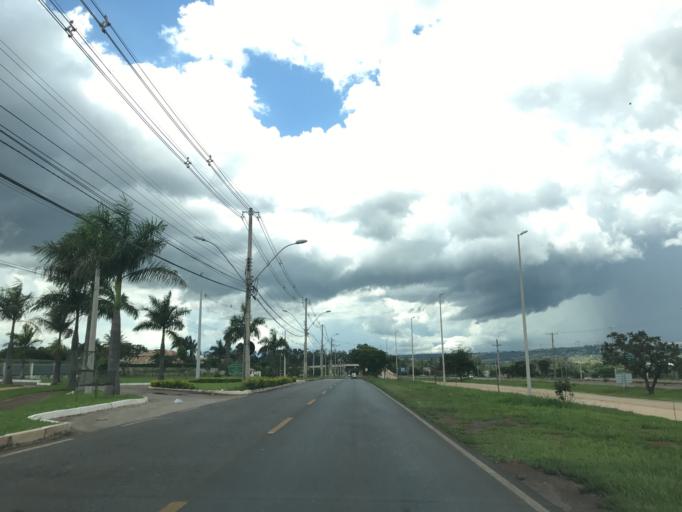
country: BR
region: Federal District
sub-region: Brasilia
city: Brasilia
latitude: -15.8741
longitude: -47.9546
